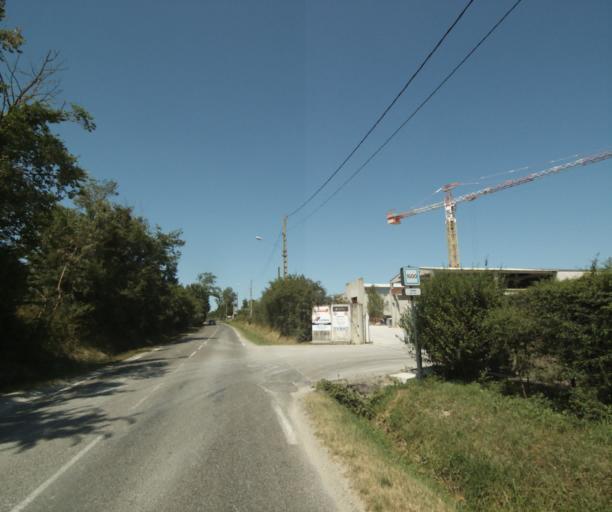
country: FR
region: Midi-Pyrenees
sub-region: Departement du Tarn-et-Garonne
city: Montauban
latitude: 44.0409
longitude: 1.3675
